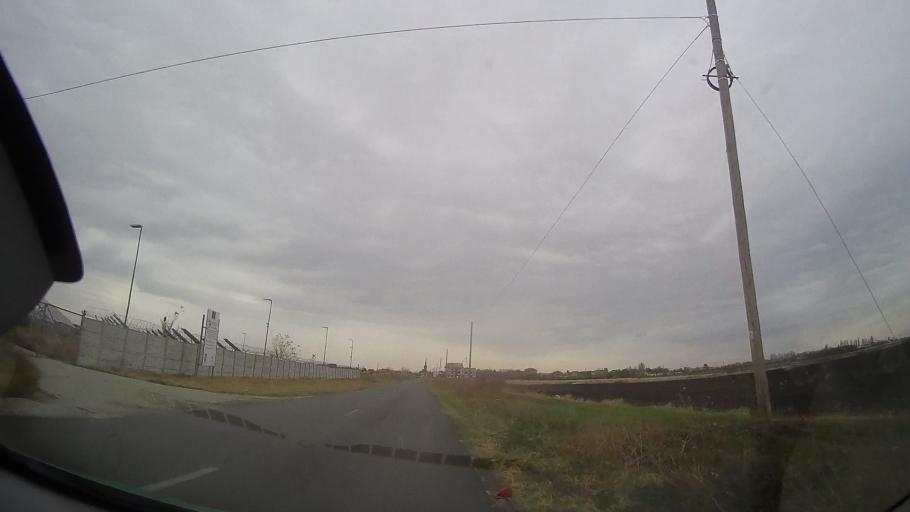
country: RO
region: Prahova
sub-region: Oras Mizil
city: Mizil
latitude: 45.0058
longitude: 26.4258
